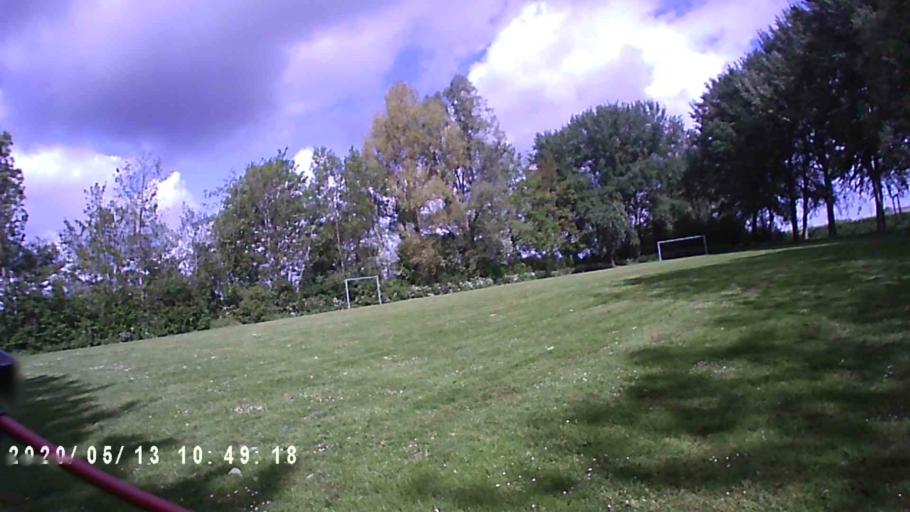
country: NL
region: Groningen
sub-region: Gemeente Zuidhorn
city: Grijpskerk
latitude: 53.2683
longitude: 6.3371
